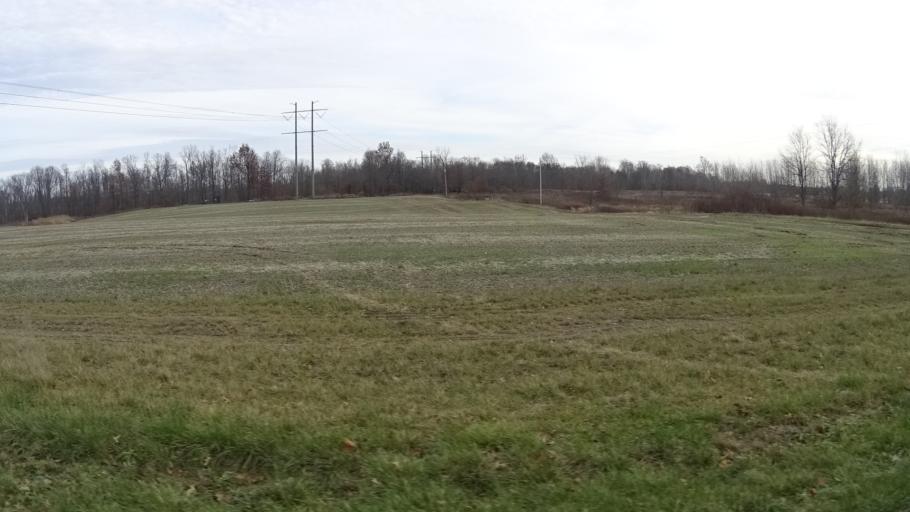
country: US
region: Ohio
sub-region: Cuyahoga County
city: Olmsted Falls
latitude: 41.3396
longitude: -81.9051
